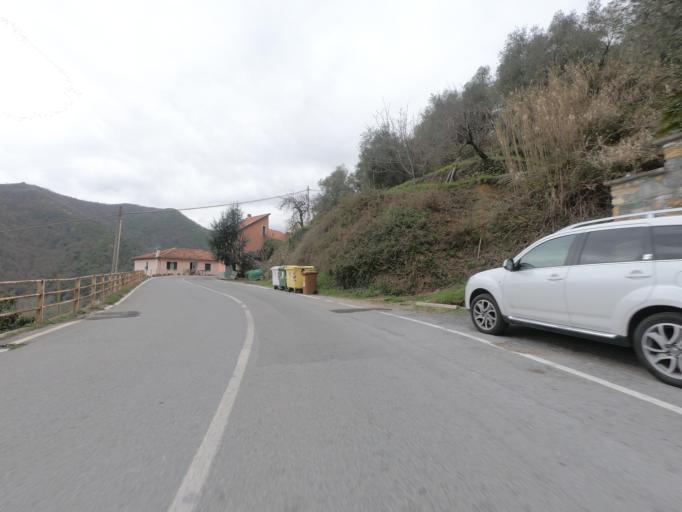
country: IT
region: Liguria
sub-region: Provincia di Savona
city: Casanova Lerrone
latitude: 44.0316
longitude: 8.0386
